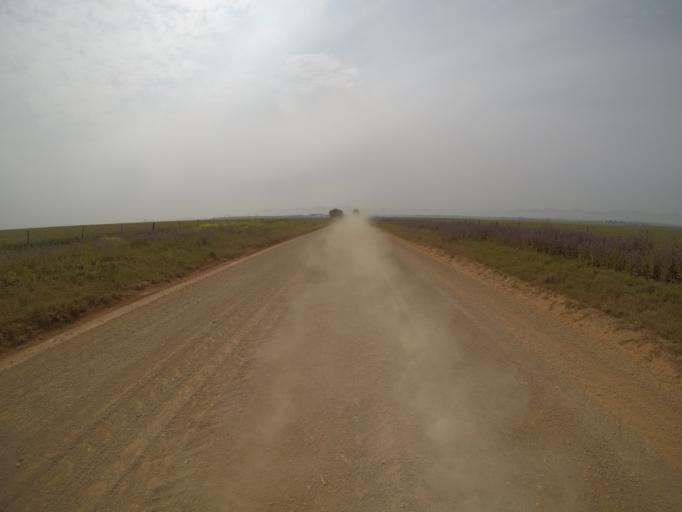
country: ZA
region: Western Cape
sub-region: City of Cape Town
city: Kraaifontein
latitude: -33.7202
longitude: 18.6770
